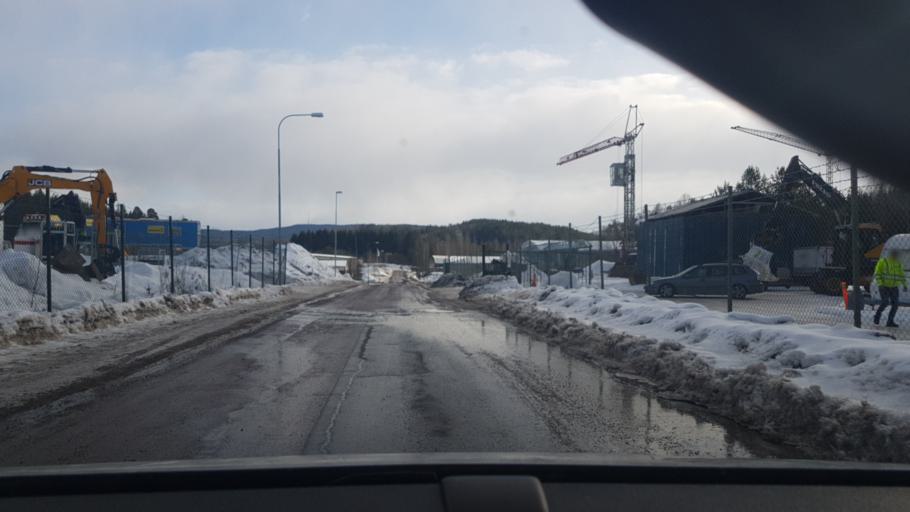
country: SE
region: Vaermland
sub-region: Arvika Kommun
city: Arvika
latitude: 59.6671
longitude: 12.6302
